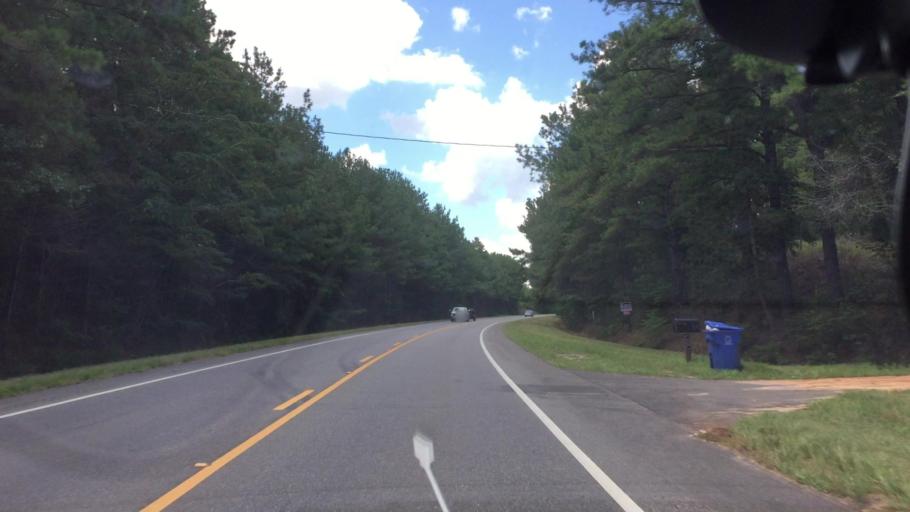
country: US
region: Alabama
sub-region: Pike County
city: Brundidge
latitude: 31.5947
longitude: -85.9452
